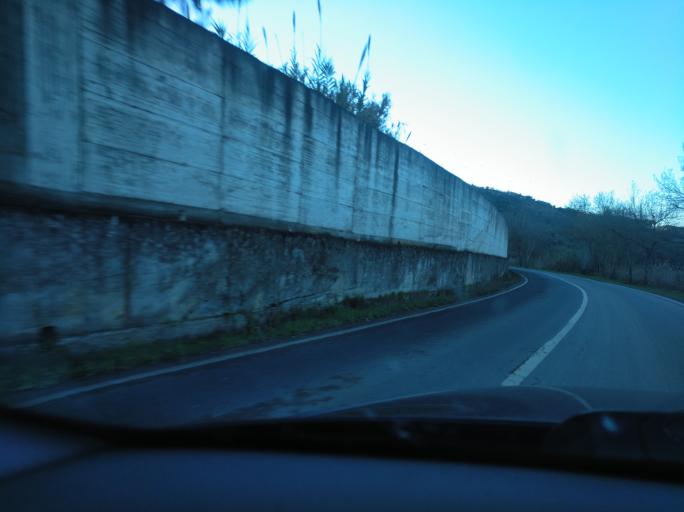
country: PT
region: Lisbon
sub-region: Loures
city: Bobadela
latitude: 38.8103
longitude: -9.1095
